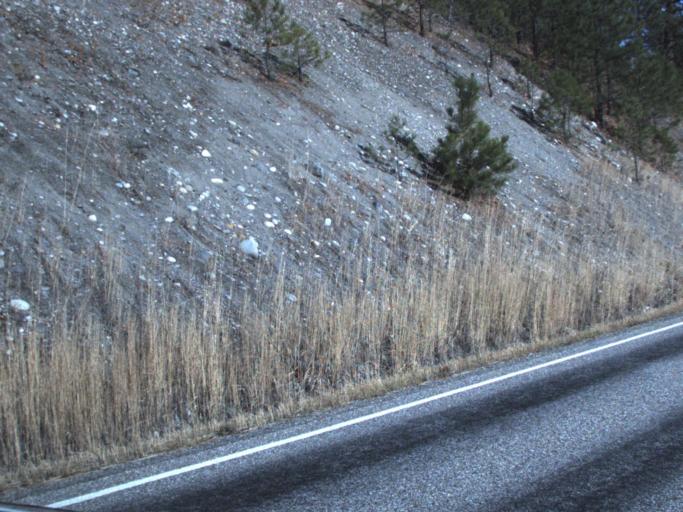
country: US
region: Washington
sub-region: Ferry County
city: Republic
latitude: 48.7859
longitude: -118.6202
